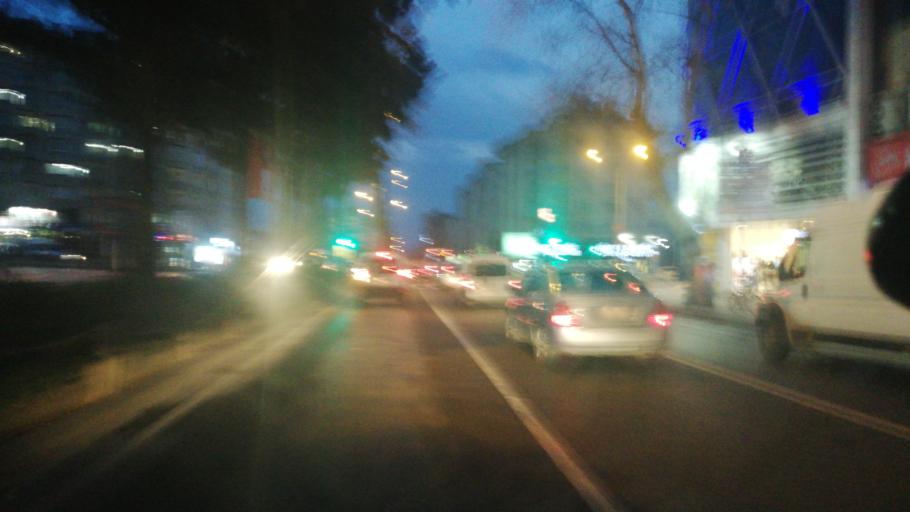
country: TR
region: Kahramanmaras
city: Kahramanmaras
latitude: 37.5762
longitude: 36.9279
